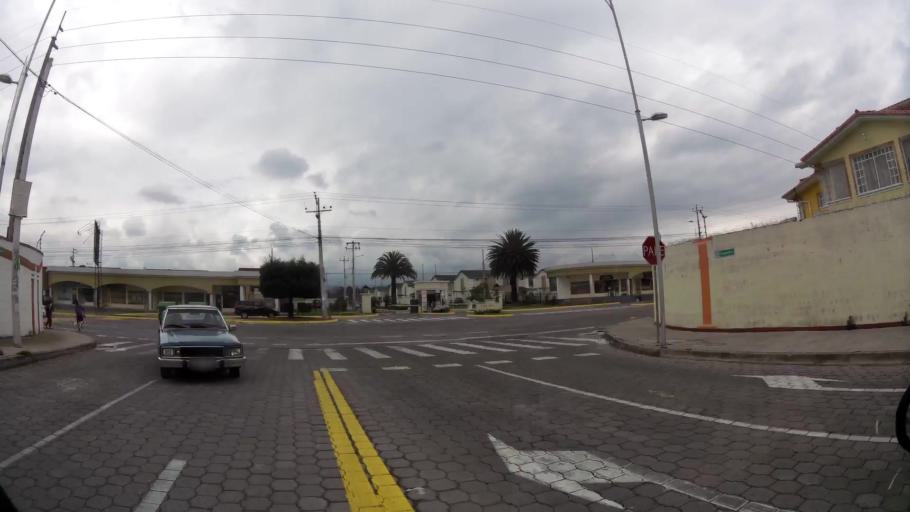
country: EC
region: Pichincha
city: Sangolqui
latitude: -0.3315
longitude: -78.4650
